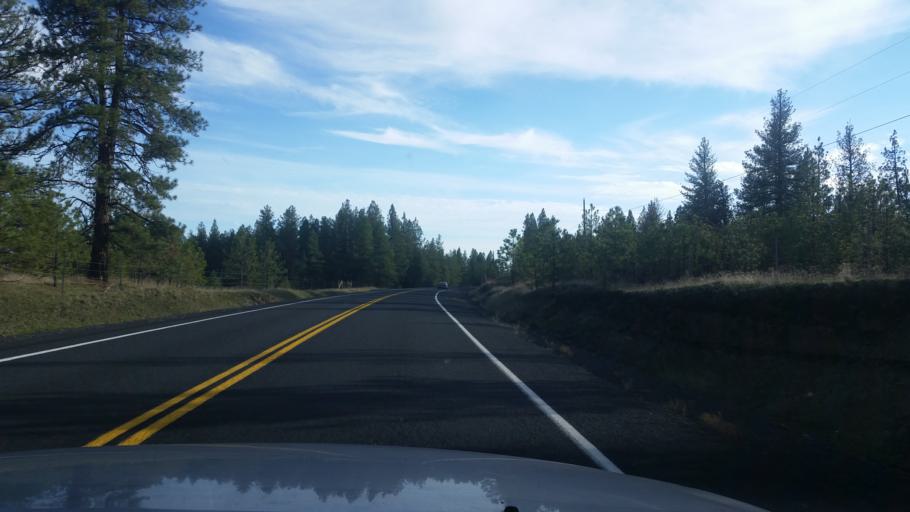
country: US
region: Washington
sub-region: Spokane County
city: Cheney
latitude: 47.3601
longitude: -117.5888
